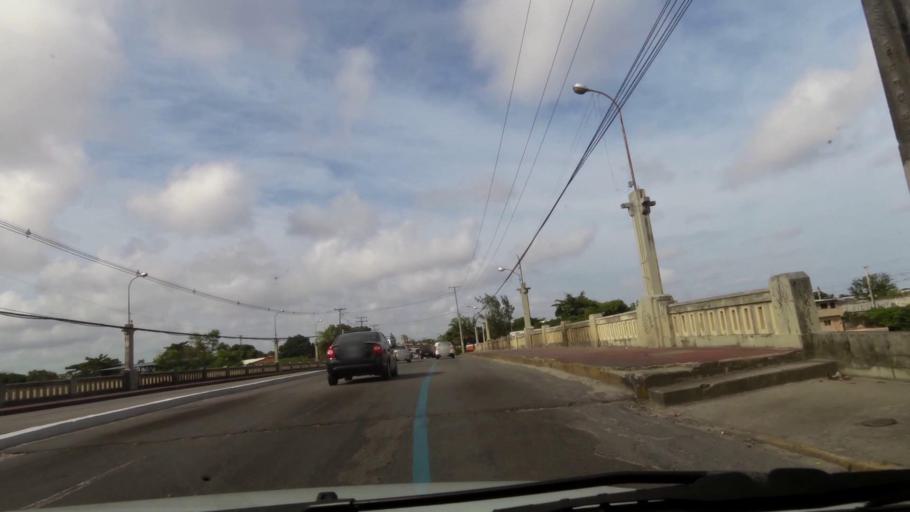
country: BR
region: Pernambuco
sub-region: Recife
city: Recife
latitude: -8.0820
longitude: -34.9056
